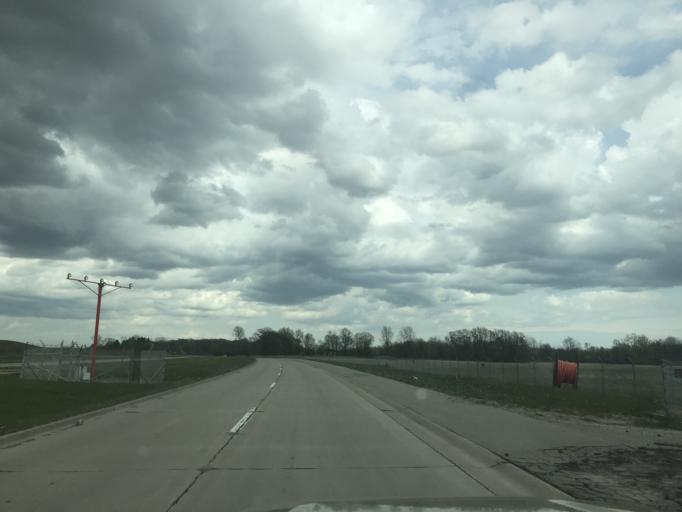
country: US
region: Michigan
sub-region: Wayne County
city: Romulus
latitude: 42.1909
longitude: -83.3557
